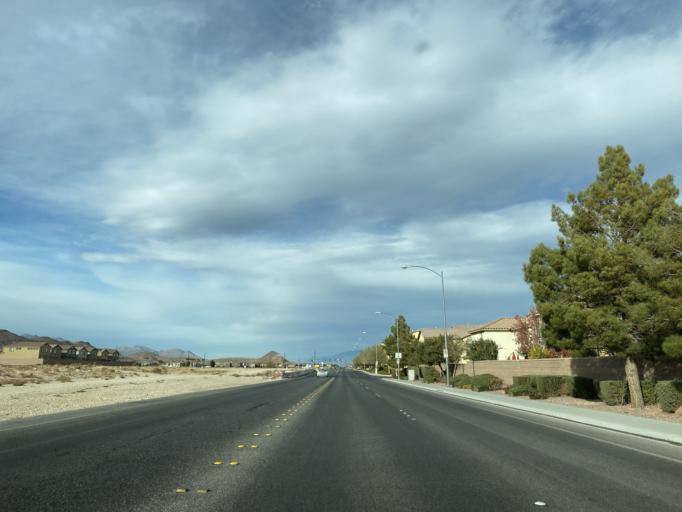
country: US
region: Nevada
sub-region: Clark County
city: Enterprise
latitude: 36.0165
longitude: -115.2980
